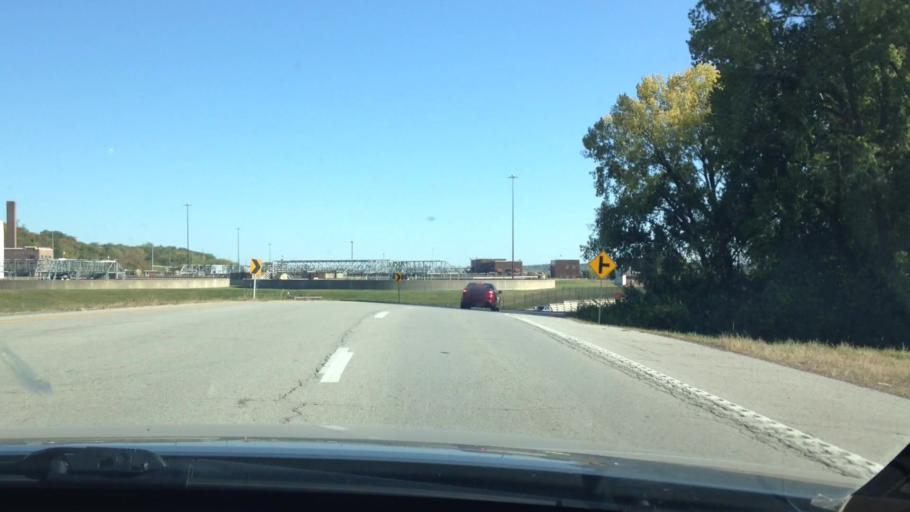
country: US
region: Missouri
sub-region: Platte County
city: Riverside
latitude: 39.1580
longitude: -94.5879
